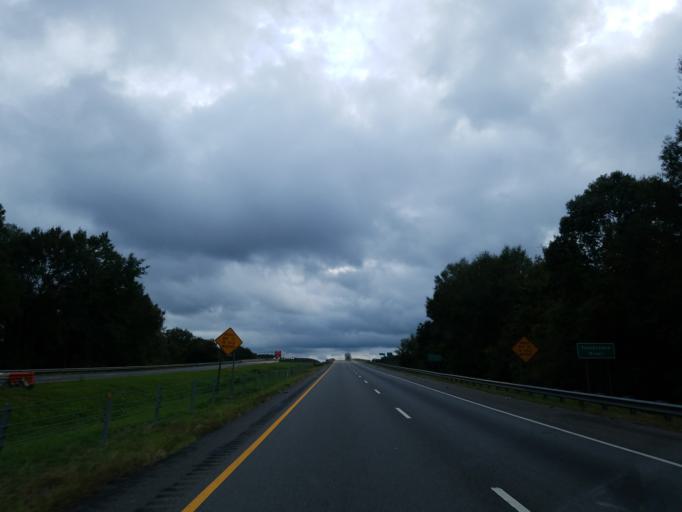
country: US
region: Alabama
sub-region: Sumter County
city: Livingston
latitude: 32.7406
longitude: -88.0952
